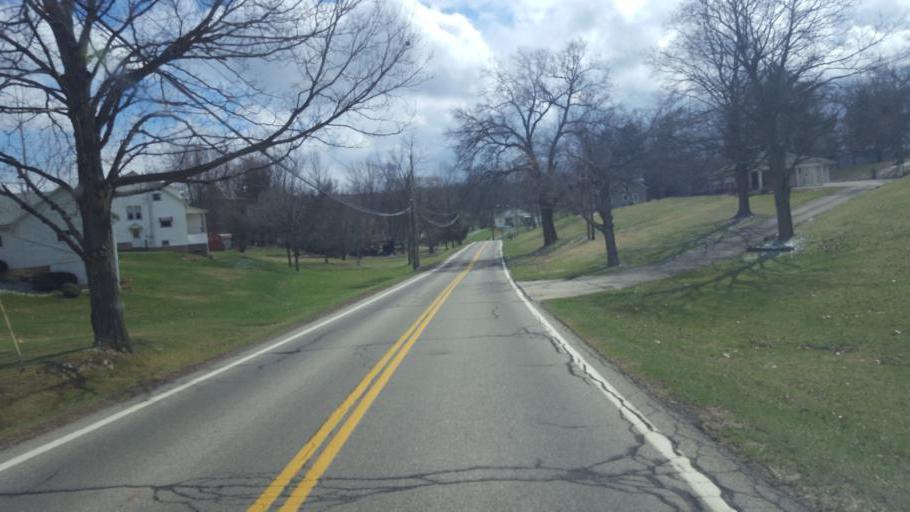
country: US
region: Ohio
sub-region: Tuscarawas County
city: Sugarcreek
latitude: 40.4425
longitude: -81.7082
